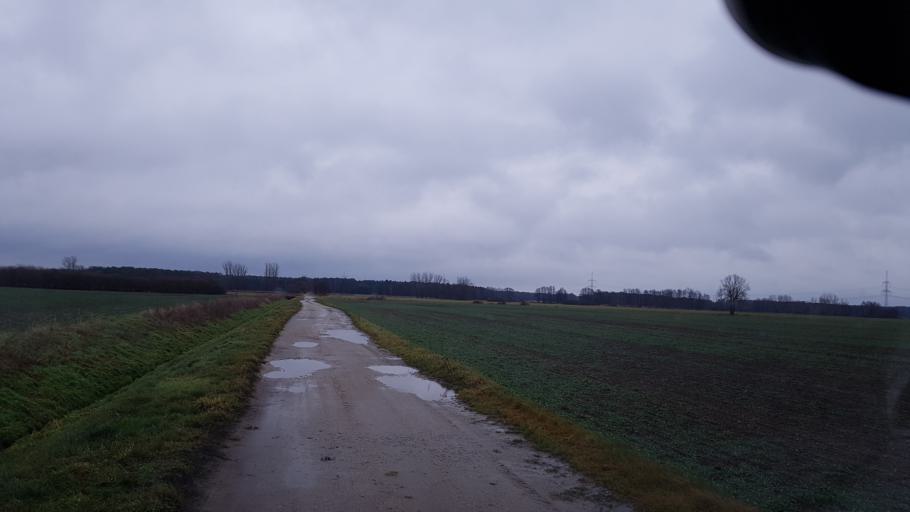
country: DE
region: Brandenburg
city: Sallgast
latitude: 51.6378
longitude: 13.8653
